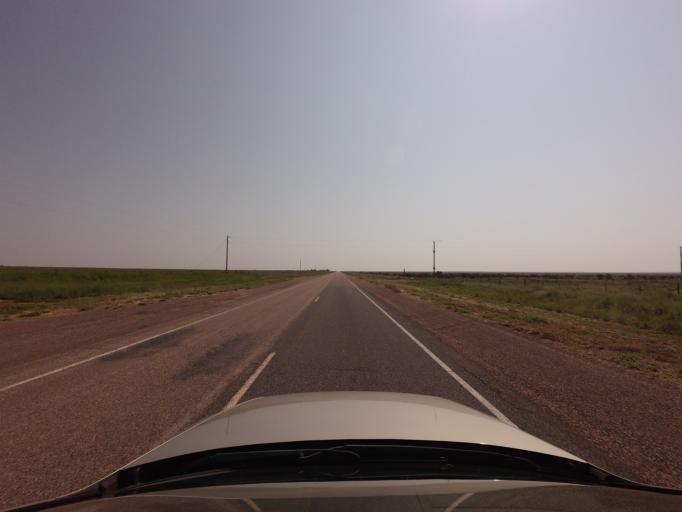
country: US
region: New Mexico
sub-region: Quay County
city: Tucumcari
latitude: 34.8234
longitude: -103.7252
